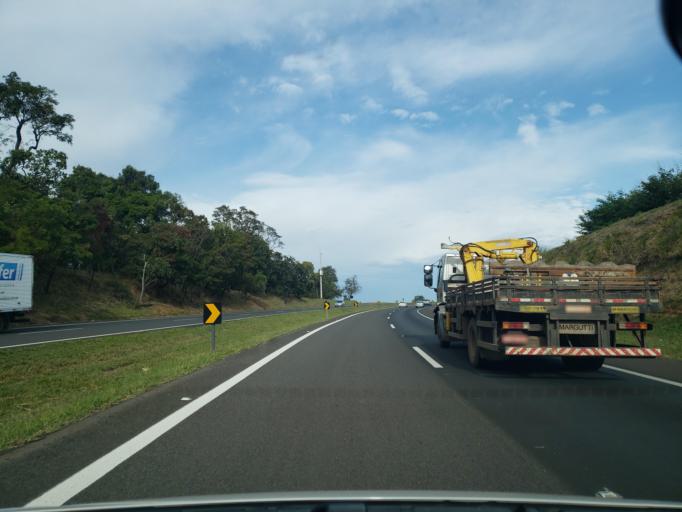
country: BR
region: Sao Paulo
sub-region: Brotas
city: Brotas
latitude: -22.2828
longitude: -47.9901
